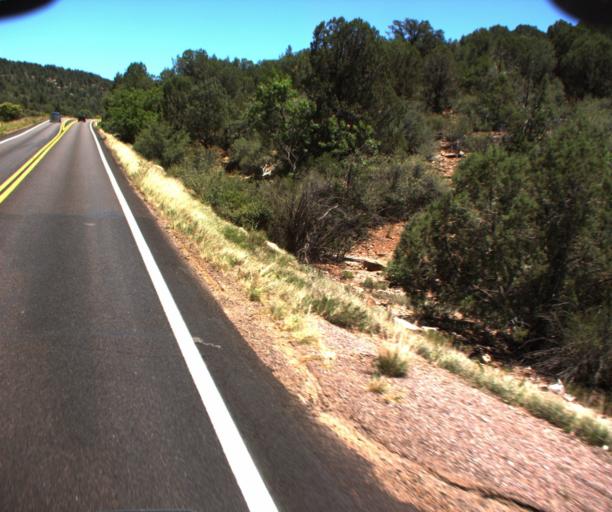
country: US
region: Arizona
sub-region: Gila County
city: Payson
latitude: 34.2955
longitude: -111.3533
